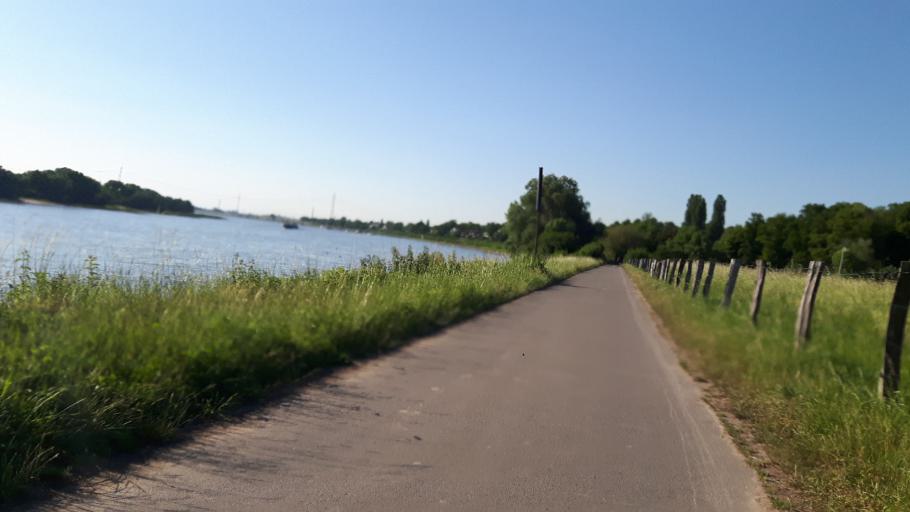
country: DE
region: North Rhine-Westphalia
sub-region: Regierungsbezirk Dusseldorf
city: Meerbusch
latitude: 51.3201
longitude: 6.7362
